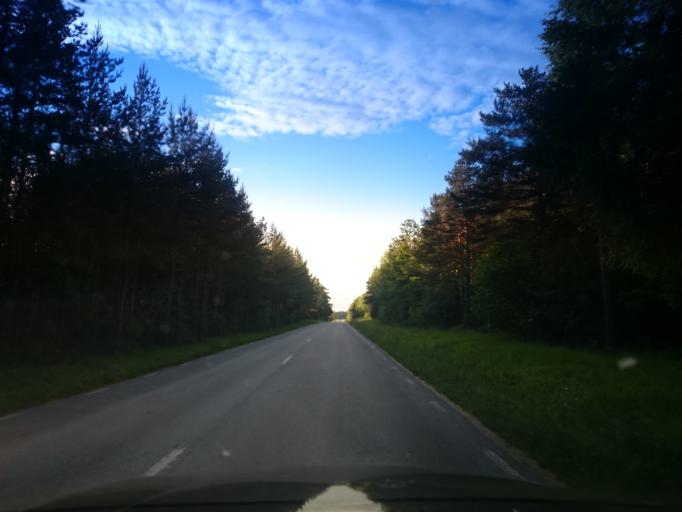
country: SE
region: Gotland
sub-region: Gotland
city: Hemse
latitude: 57.2977
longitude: 18.3843
